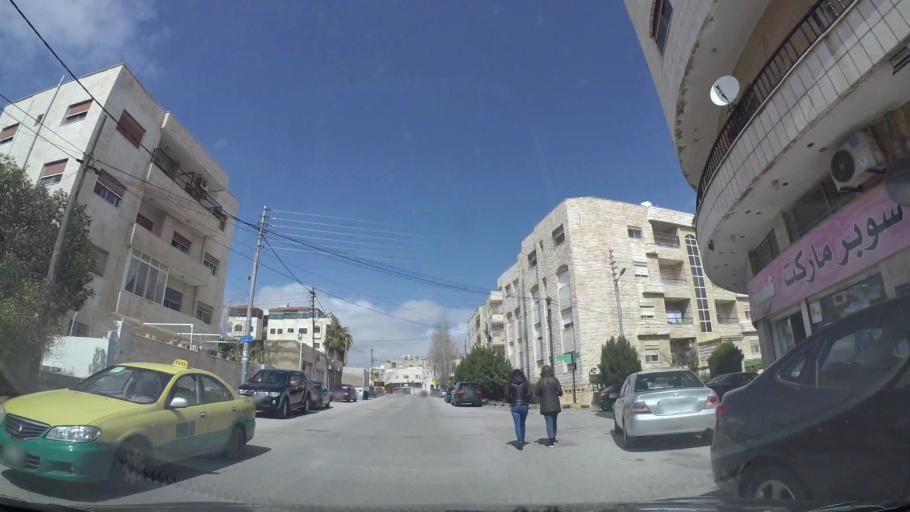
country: JO
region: Amman
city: Wadi as Sir
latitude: 31.9557
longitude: 35.8394
